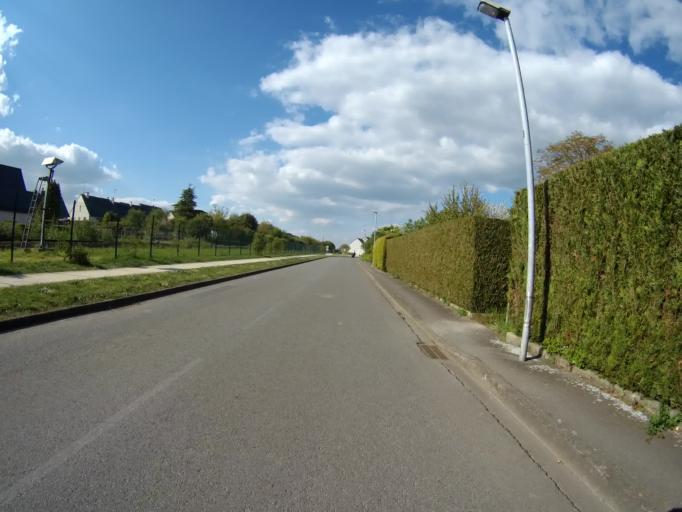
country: FR
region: Brittany
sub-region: Departement d'Ille-et-Vilaine
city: Vern-sur-Seiche
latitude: 48.0438
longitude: -1.5963
